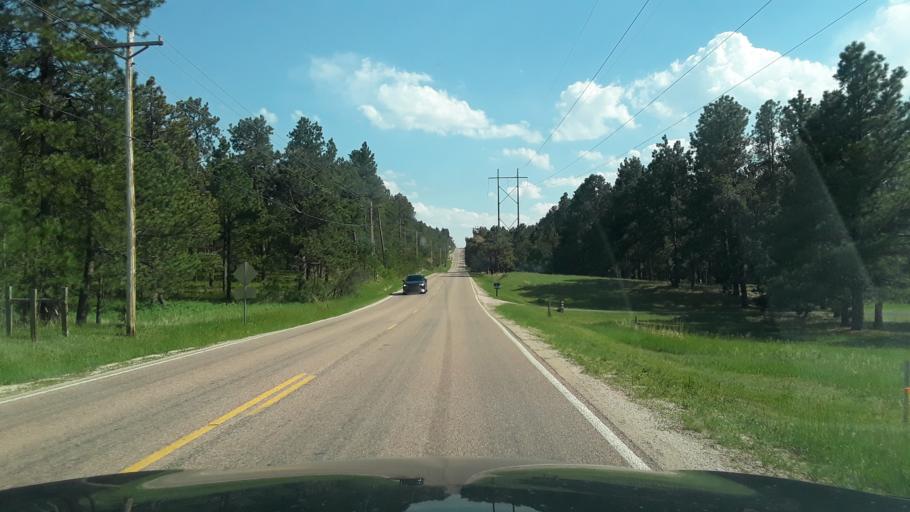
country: US
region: Colorado
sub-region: El Paso County
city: Gleneagle
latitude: 39.0557
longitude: -104.7849
